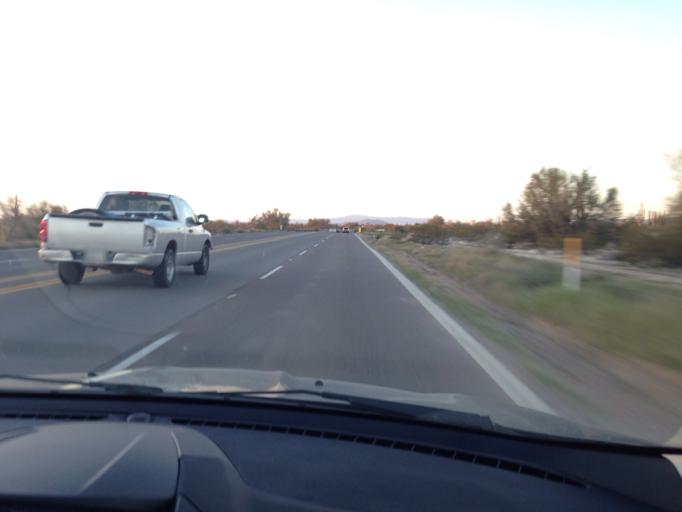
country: US
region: Arizona
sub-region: Maricopa County
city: Carefree
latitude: 33.7100
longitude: -111.9730
